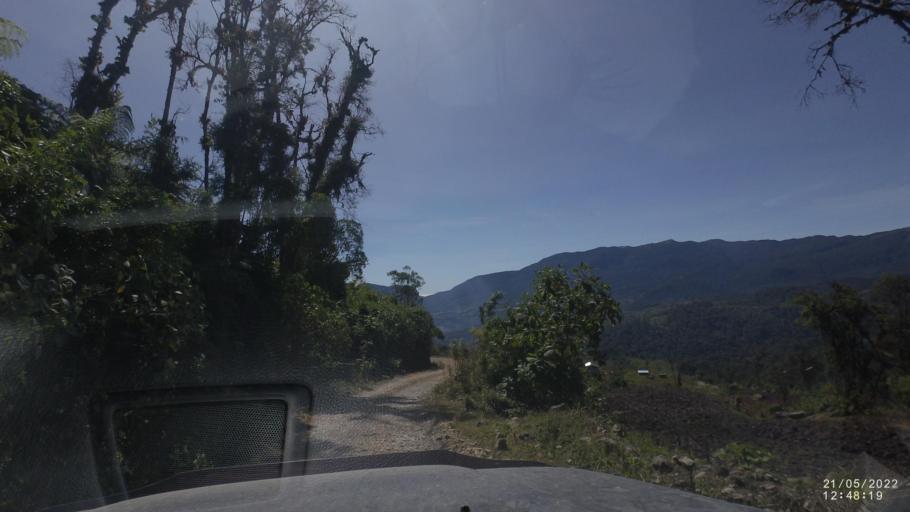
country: BO
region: Cochabamba
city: Colomi
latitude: -17.1804
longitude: -65.9427
